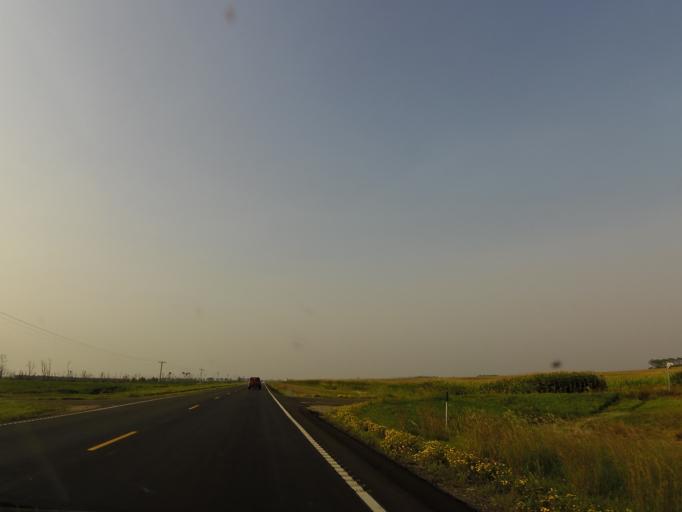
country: US
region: North Dakota
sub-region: Traill County
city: Mayville
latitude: 47.4106
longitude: -97.3262
